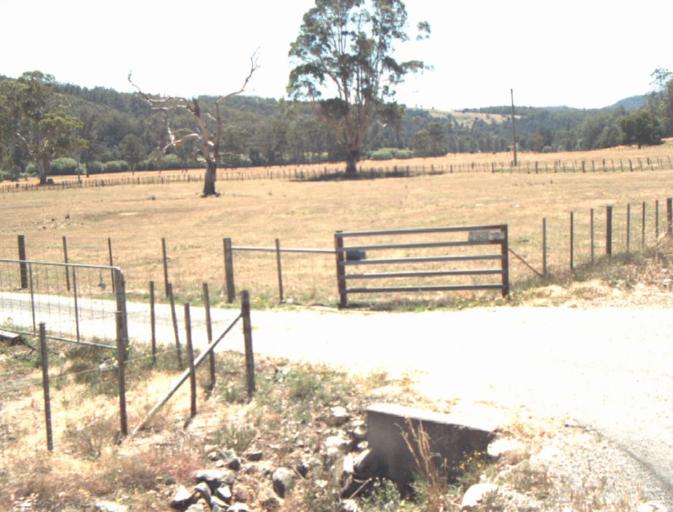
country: AU
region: Tasmania
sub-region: Launceston
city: Newstead
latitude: -41.3241
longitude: 147.3604
